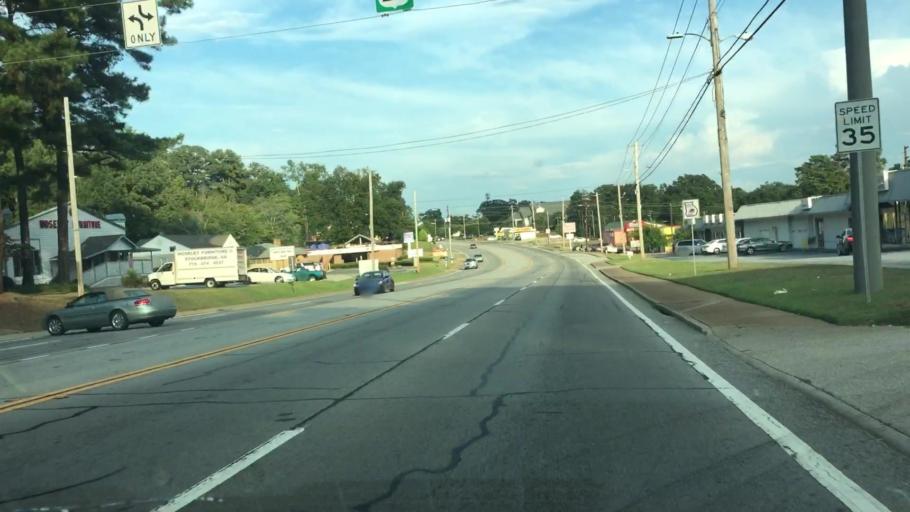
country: US
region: Georgia
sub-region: Henry County
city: Stockbridge
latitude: 33.5448
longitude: -84.2440
